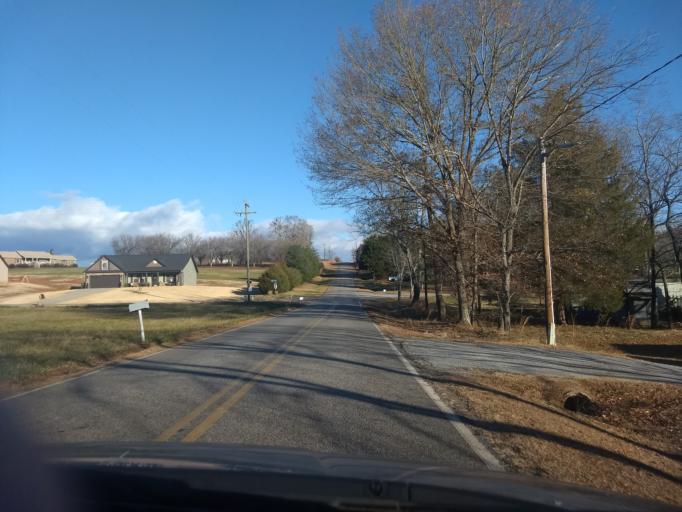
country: US
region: South Carolina
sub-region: Greenville County
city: Greer
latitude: 35.0260
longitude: -82.2016
